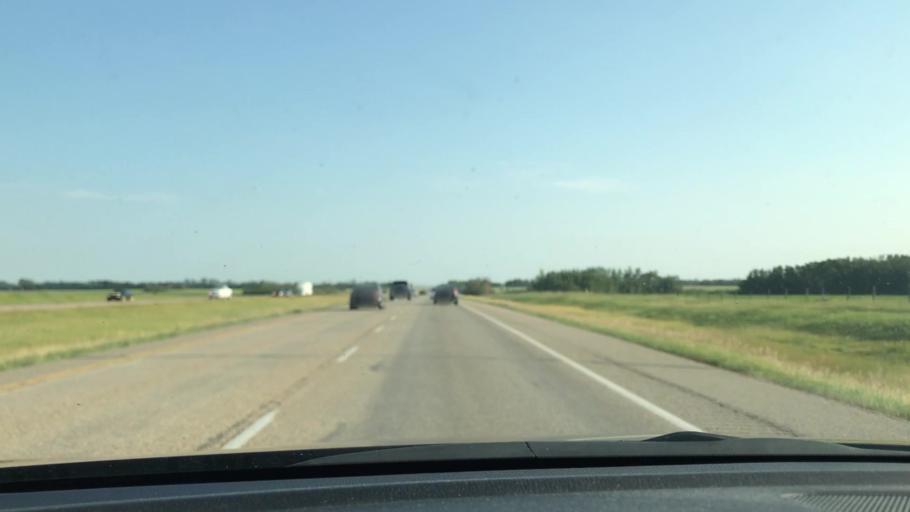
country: CA
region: Alberta
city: Millet
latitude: 53.1247
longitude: -113.5984
